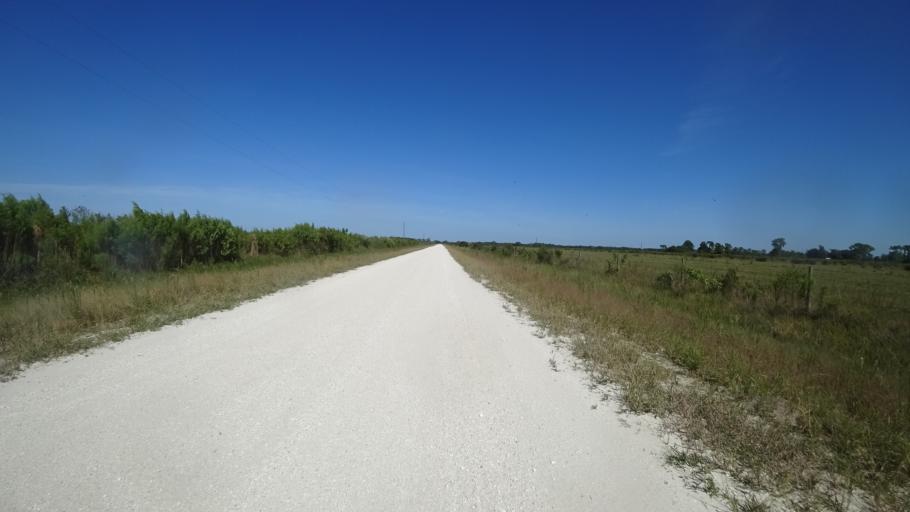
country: US
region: Florida
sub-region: DeSoto County
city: Arcadia
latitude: 27.3331
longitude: -82.0806
